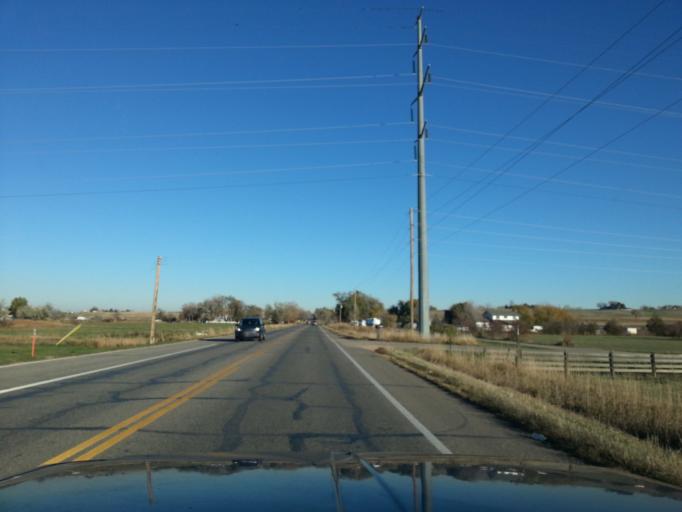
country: US
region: Colorado
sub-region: Larimer County
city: Loveland
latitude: 40.3783
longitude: -105.0409
